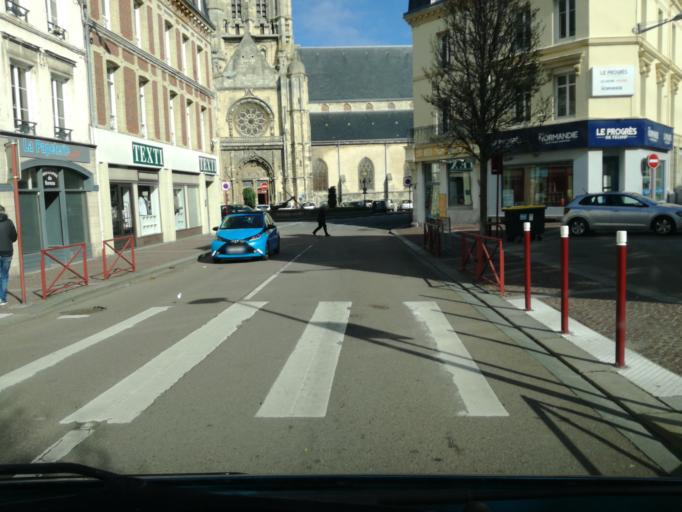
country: FR
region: Haute-Normandie
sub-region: Departement de la Seine-Maritime
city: Fecamp
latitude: 49.7575
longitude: 0.3763
